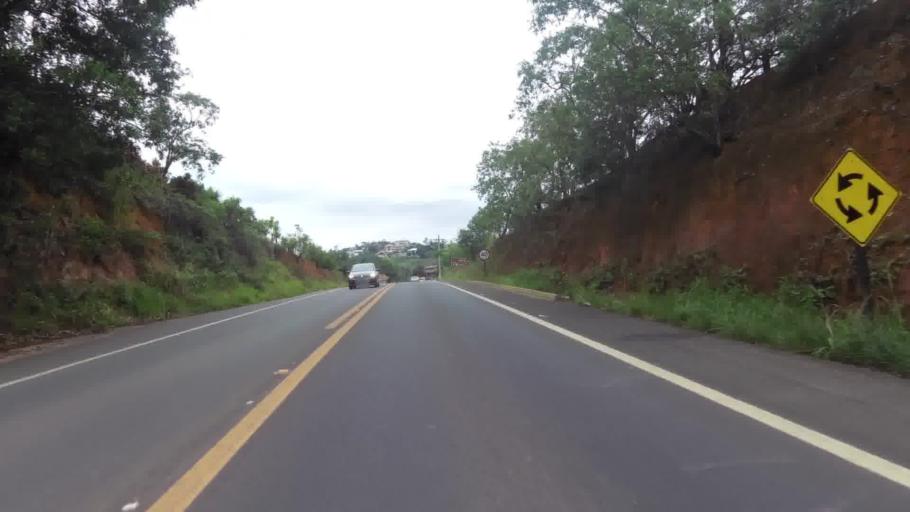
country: BR
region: Espirito Santo
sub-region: Piuma
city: Piuma
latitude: -20.8294
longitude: -40.7030
